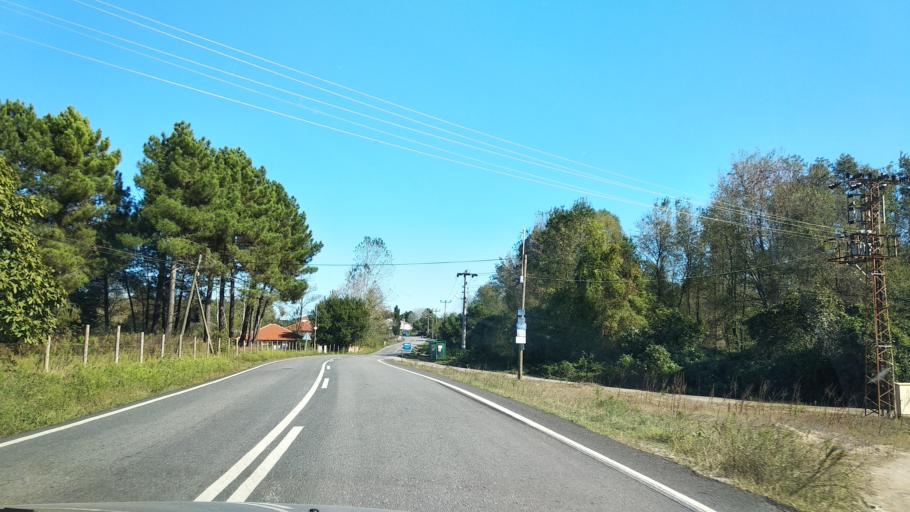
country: TR
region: Sakarya
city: Karasu
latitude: 41.1189
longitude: 30.6099
